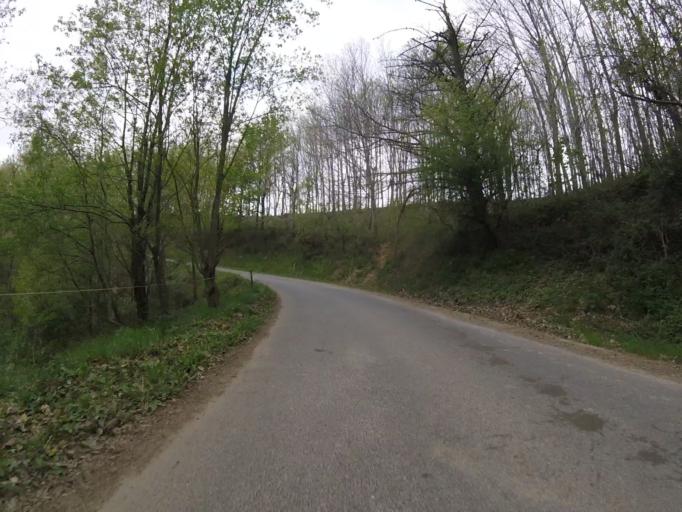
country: ES
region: Basque Country
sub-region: Provincia de Guipuzcoa
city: Zizurkil
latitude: 43.2134
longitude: -2.0845
